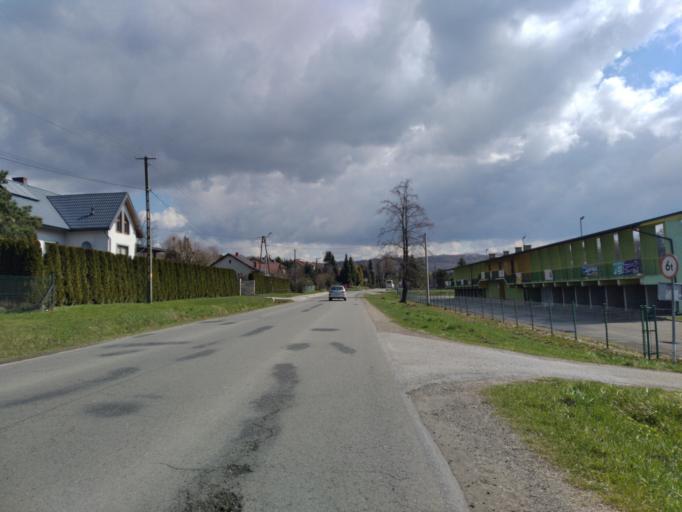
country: PL
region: Subcarpathian Voivodeship
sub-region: Powiat brzozowski
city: Niebocko
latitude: 49.6764
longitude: 22.1024
